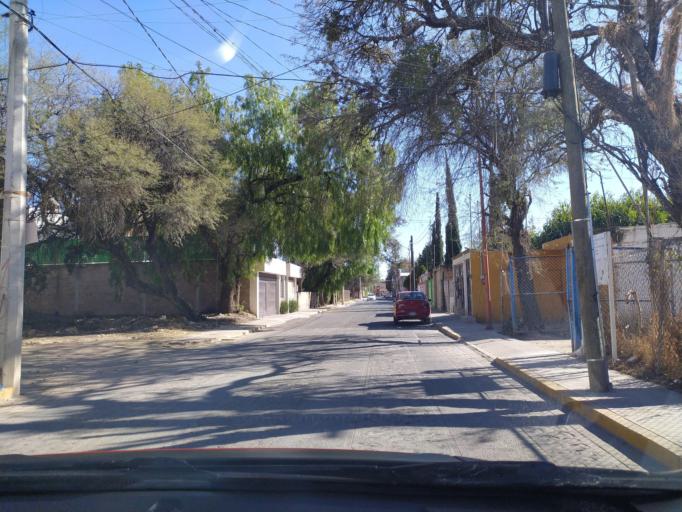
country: MX
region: Guanajuato
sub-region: San Francisco del Rincon
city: Estacion de San Francisco
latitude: 21.0261
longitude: -101.8325
